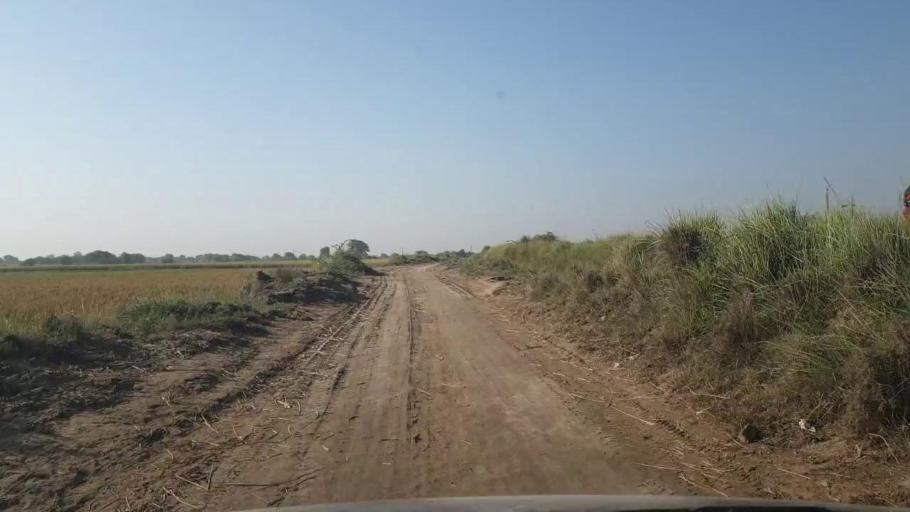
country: PK
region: Sindh
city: Badin
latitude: 24.7060
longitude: 68.7780
